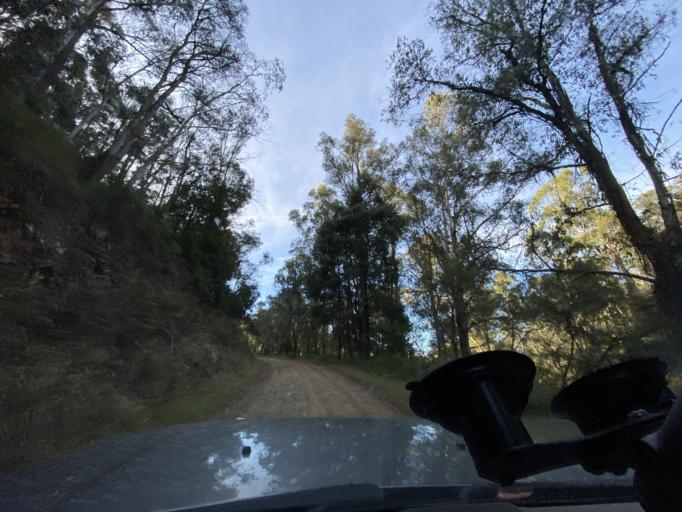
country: AU
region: Victoria
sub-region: Mansfield
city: Mansfield
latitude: -37.5193
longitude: 146.0919
